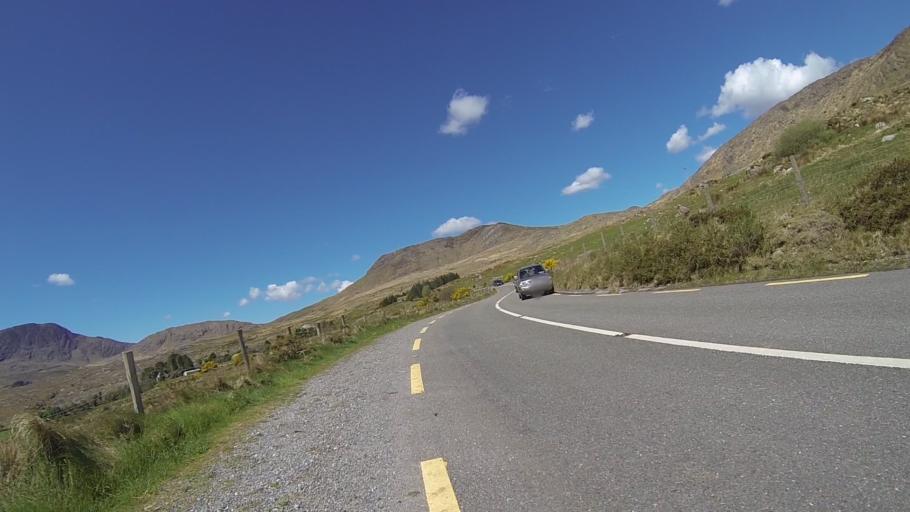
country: IE
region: Munster
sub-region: Ciarrai
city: Kenmare
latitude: 51.9221
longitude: -9.6298
